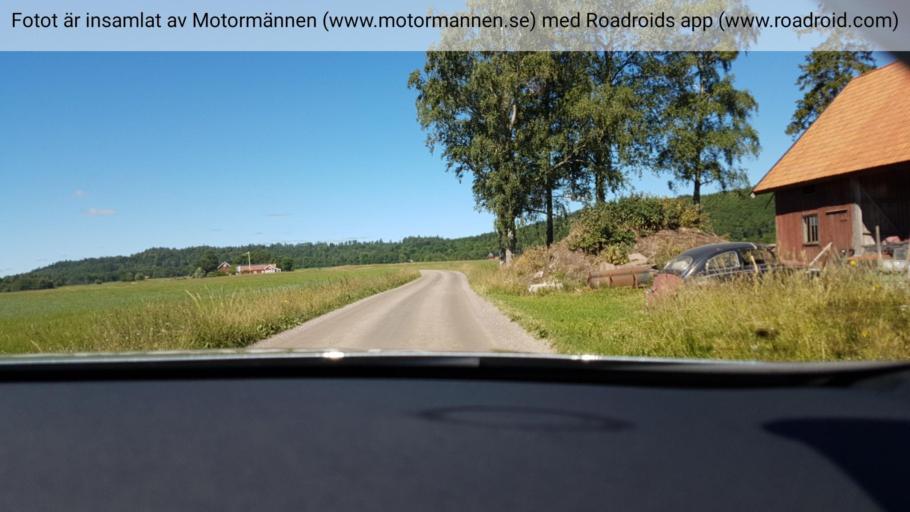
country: SE
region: Vaestra Goetaland
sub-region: Skovde Kommun
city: Skultorp
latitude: 58.2247
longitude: 13.7887
